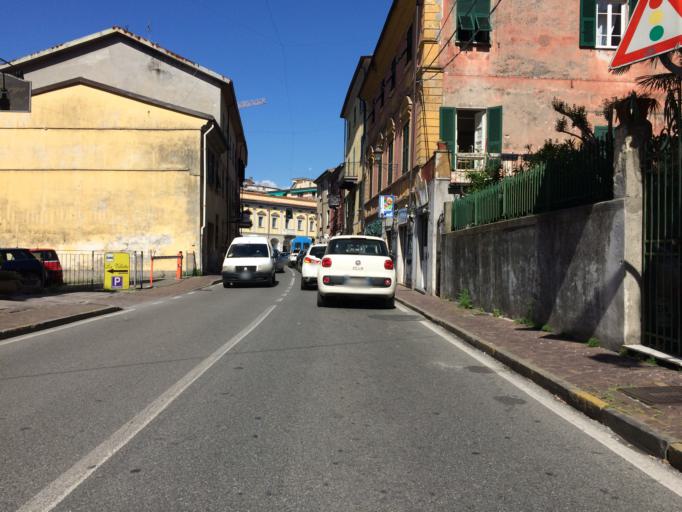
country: IT
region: Liguria
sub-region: Provincia di La Spezia
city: Sarzana
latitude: 44.1118
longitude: 9.9599
